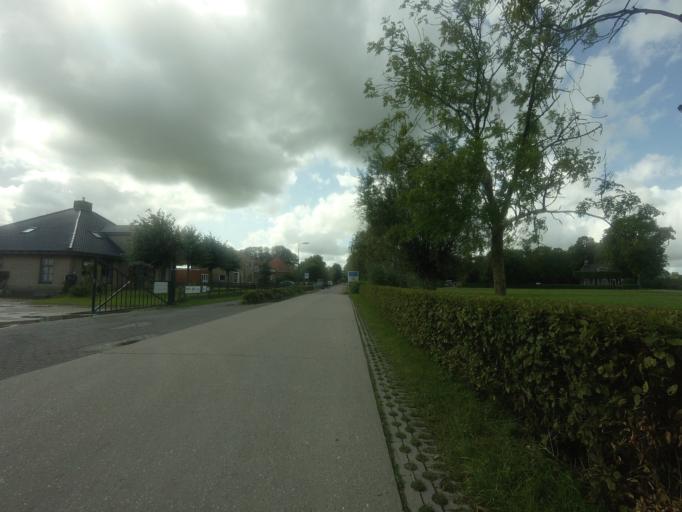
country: NL
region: Friesland
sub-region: Gemeente Littenseradiel
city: Makkum
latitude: 53.0895
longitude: 5.6999
